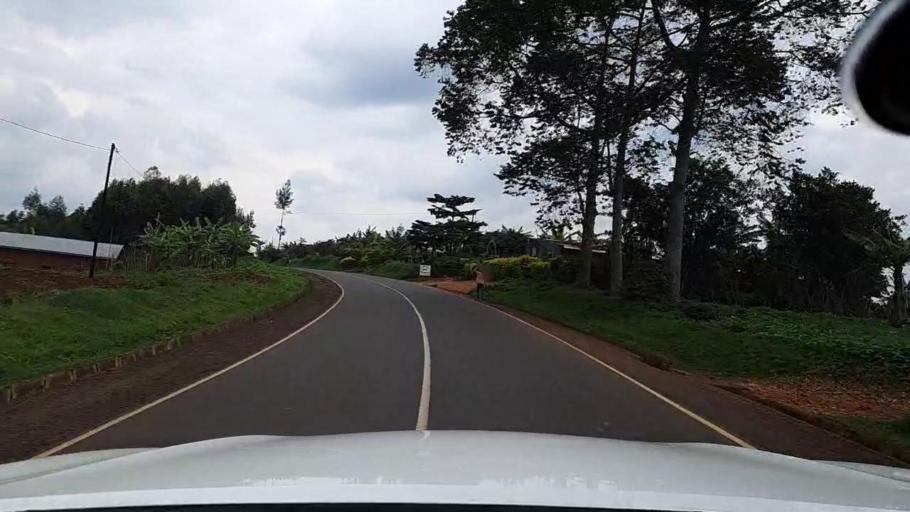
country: RW
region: Western Province
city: Cyangugu
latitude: -2.5927
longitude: 28.9246
